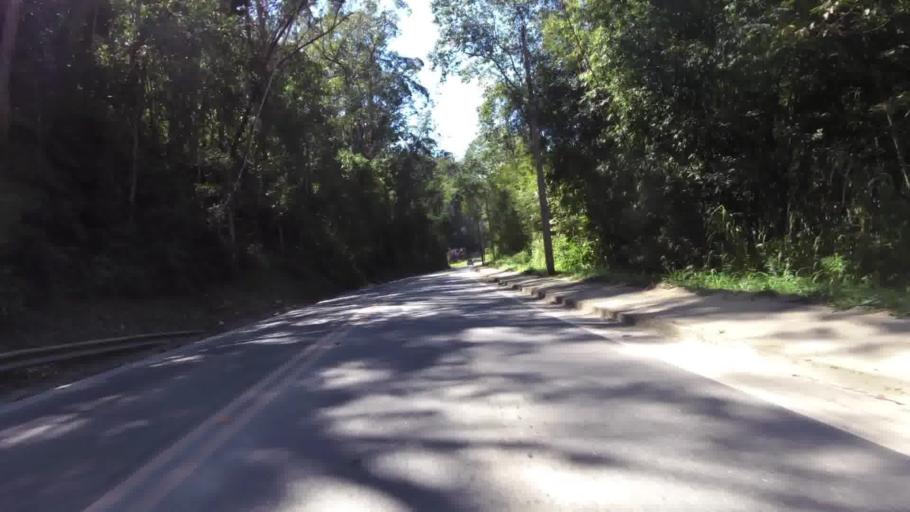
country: BR
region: Espirito Santo
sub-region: Vargem Alta
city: Vargem Alta
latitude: -20.6792
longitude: -41.0236
